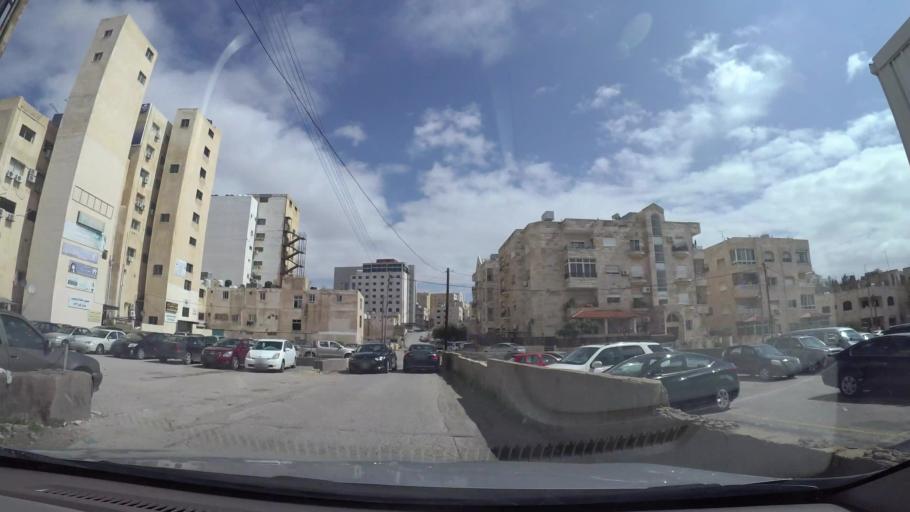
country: JO
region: Amman
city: Al Jubayhah
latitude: 31.9964
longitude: 35.8488
